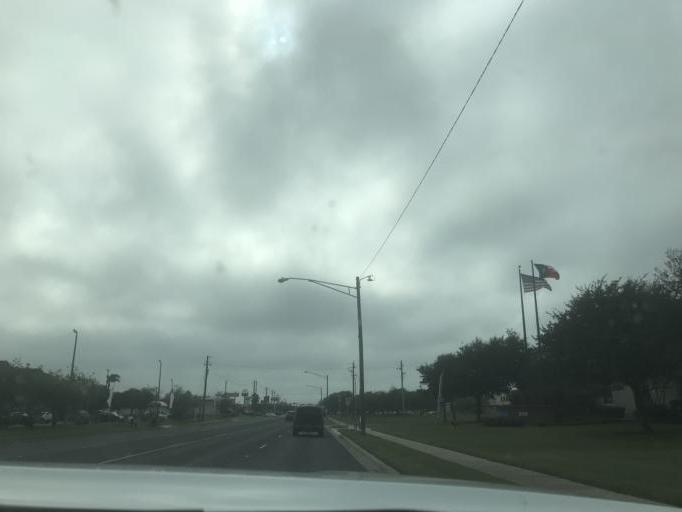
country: US
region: Texas
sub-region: Nueces County
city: Corpus Christi
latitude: 27.6810
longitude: -97.3681
